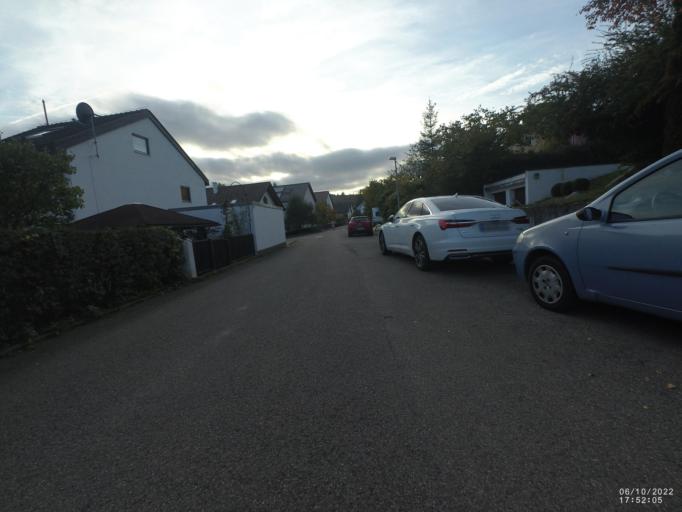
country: DE
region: Baden-Wuerttemberg
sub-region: Regierungsbezirk Stuttgart
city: Ebersbach an der Fils
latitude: 48.7564
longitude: 9.5245
